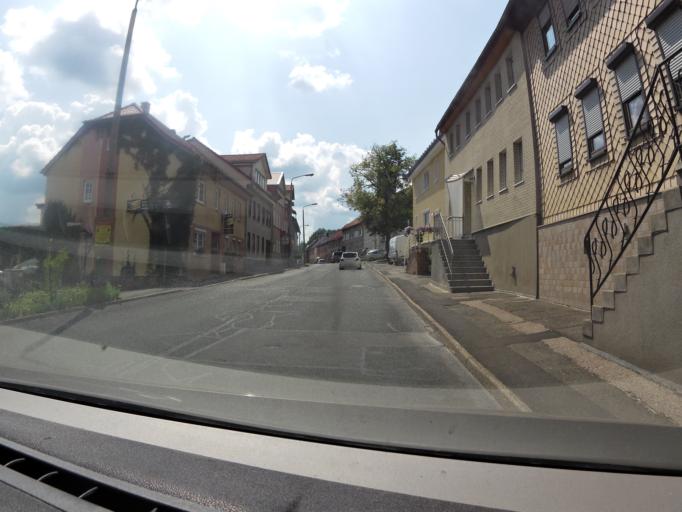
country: DE
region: Thuringia
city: Plaue
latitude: 50.7790
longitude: 10.8984
